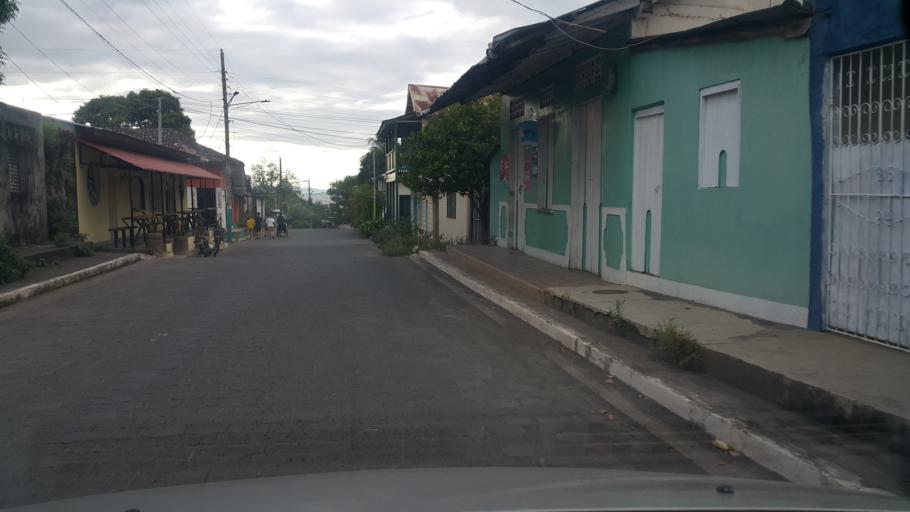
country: NI
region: Rivas
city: Moyogalpa
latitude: 11.5396
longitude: -85.6978
